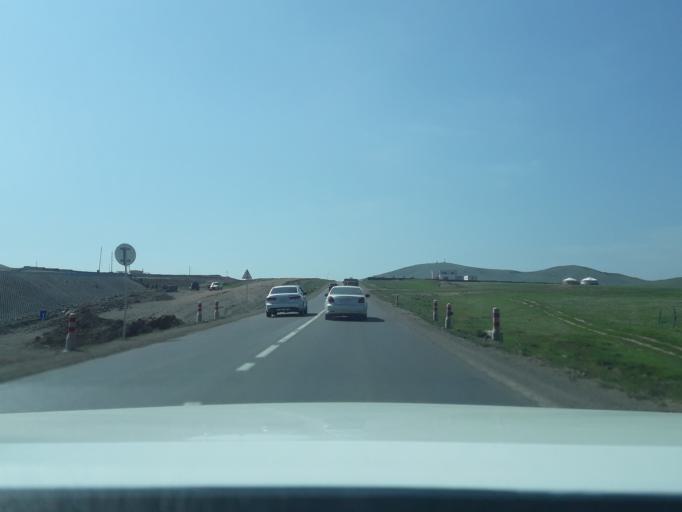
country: MN
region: Ulaanbaatar
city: Ulaanbaatar
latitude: 47.8084
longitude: 106.7511
